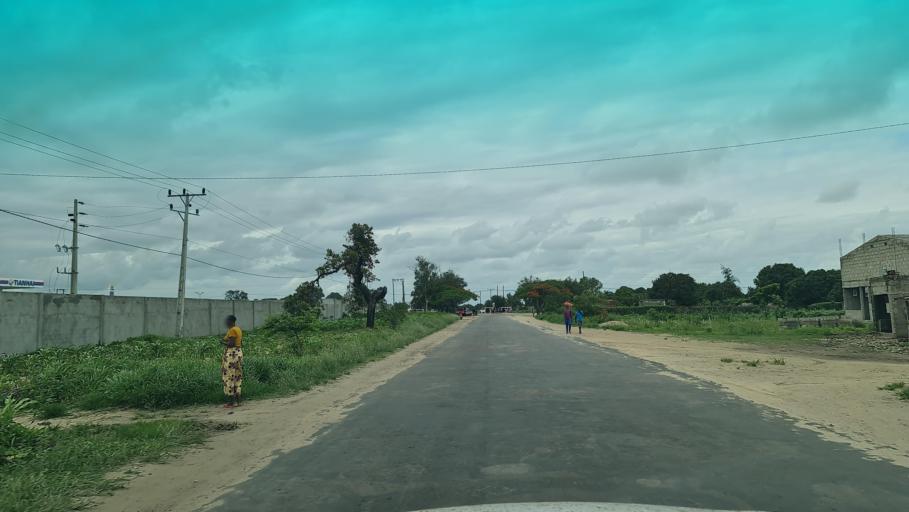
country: MZ
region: Maputo
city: Manhica
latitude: -25.4121
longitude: 32.7721
